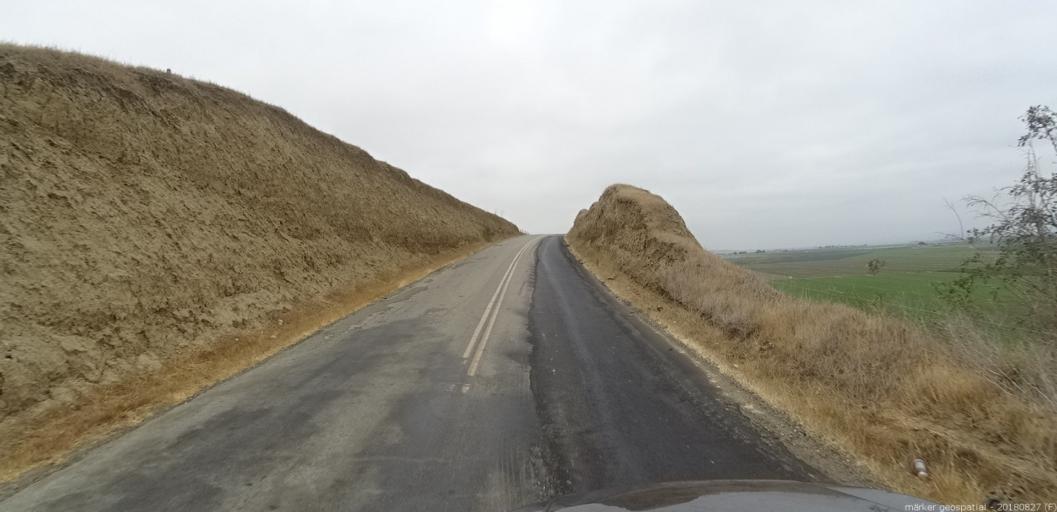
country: US
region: California
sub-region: Monterey County
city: Greenfield
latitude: 36.3155
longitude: -121.1723
